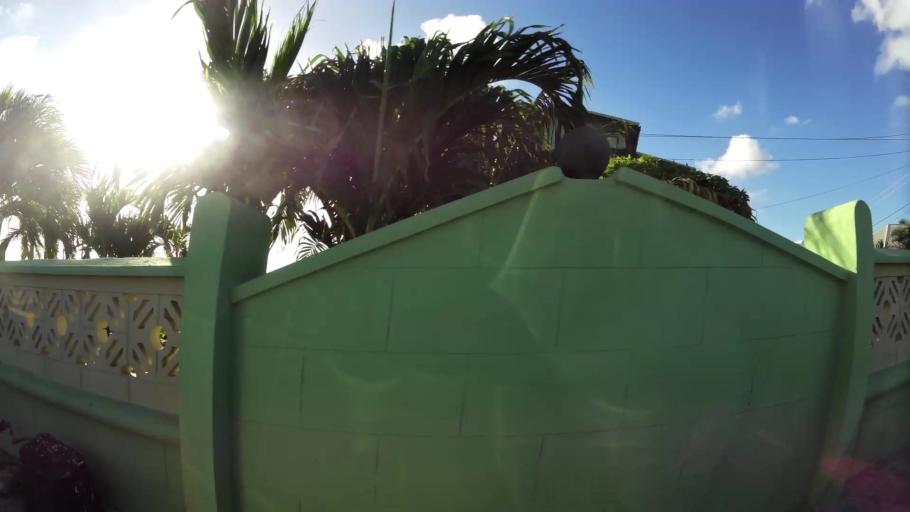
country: AG
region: Saint George
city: Piggotts
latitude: 17.1185
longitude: -61.8007
